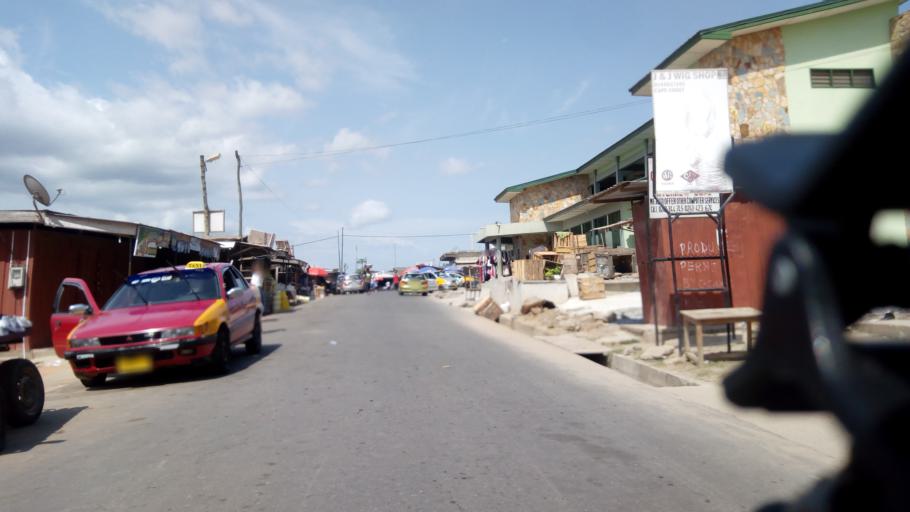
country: GH
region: Central
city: Cape Coast
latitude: 5.1328
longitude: -1.2771
